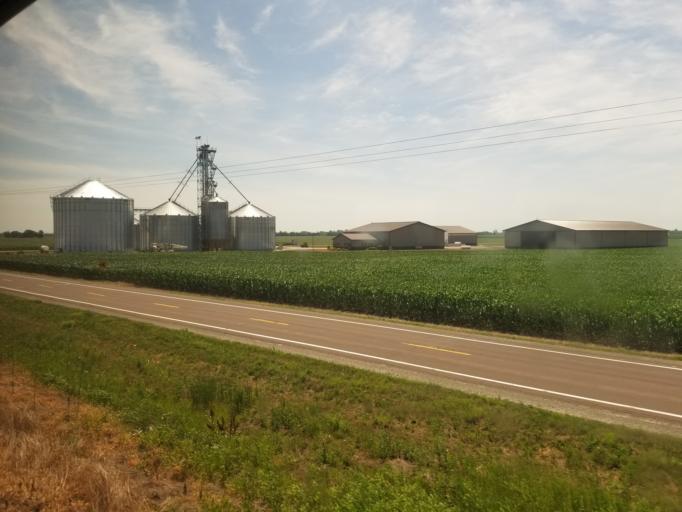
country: US
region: Missouri
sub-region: Carroll County
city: Carrollton
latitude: 39.3156
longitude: -93.6202
